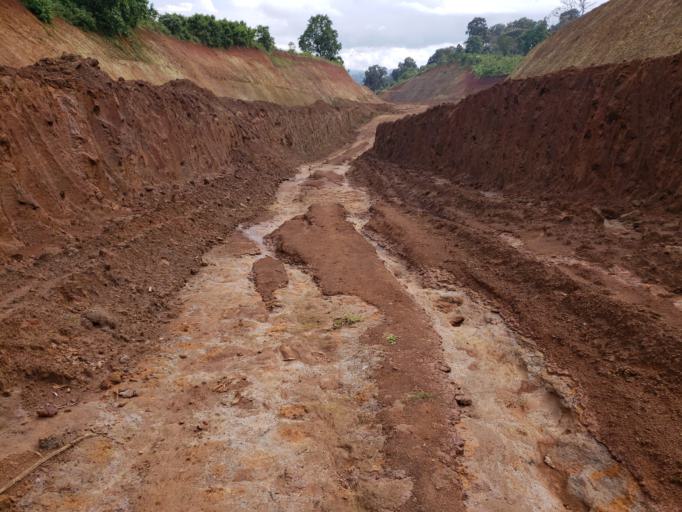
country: ET
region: Oromiya
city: Dodola
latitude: 6.5490
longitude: 39.4225
